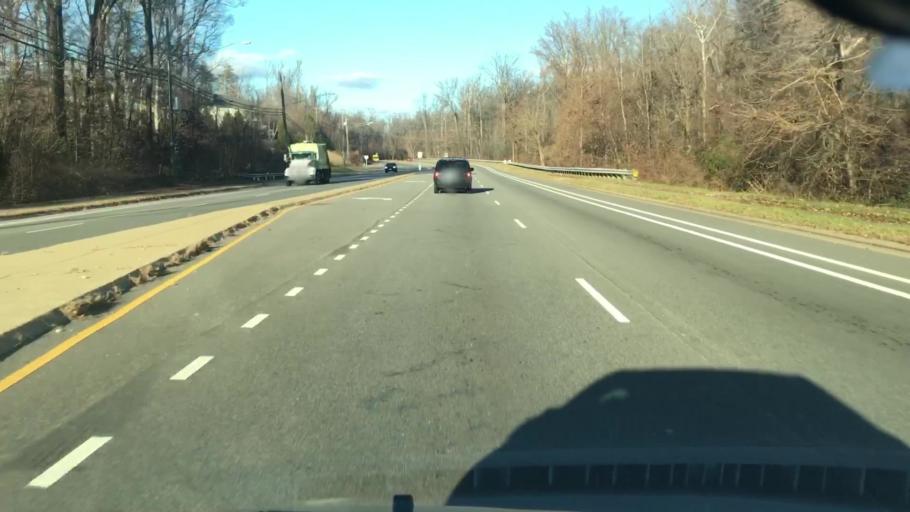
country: US
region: Virginia
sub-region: Fairfax County
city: Newington
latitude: 38.7343
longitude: -77.1701
